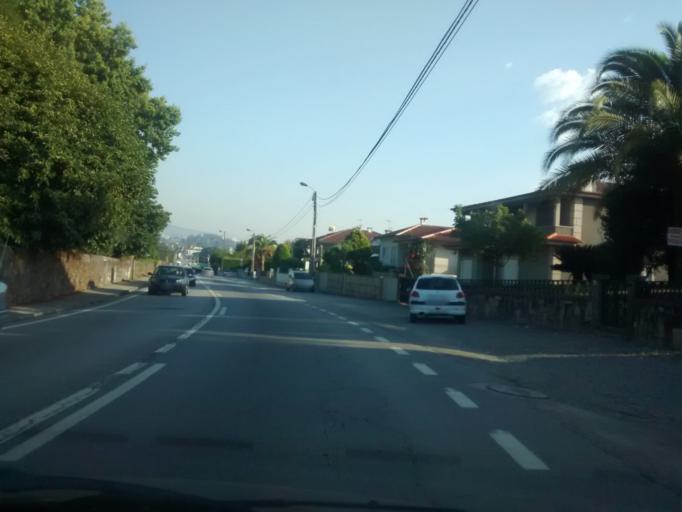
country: PT
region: Braga
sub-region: Braga
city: Adaufe
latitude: 41.5847
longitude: -8.4292
